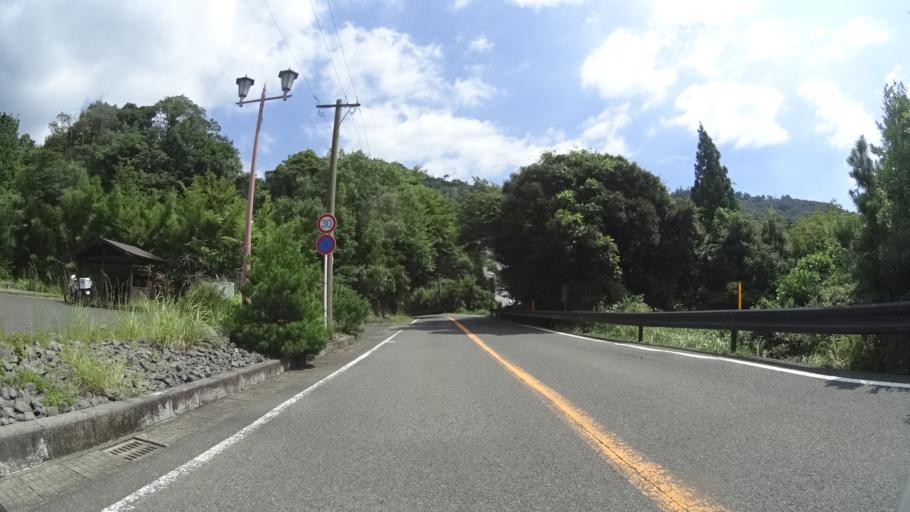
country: JP
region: Miyazaki
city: Kobayashi
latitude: 31.8980
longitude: 130.8351
